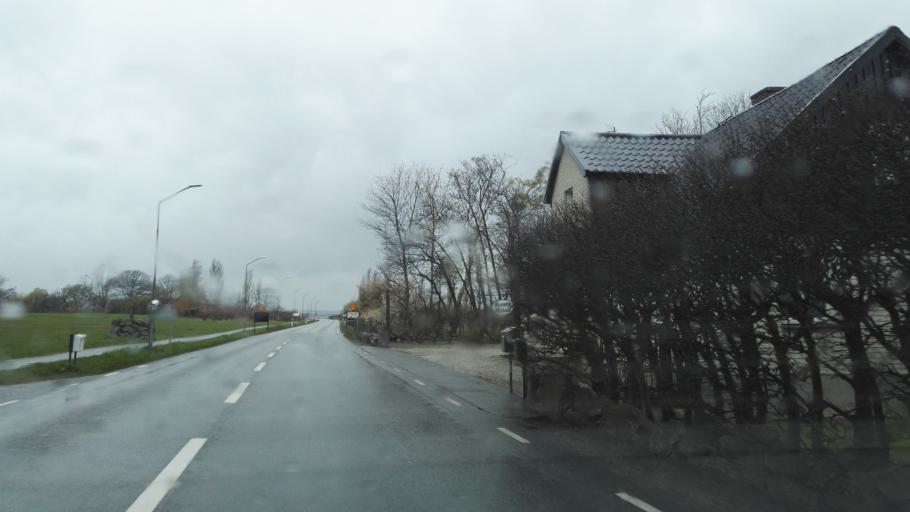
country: SE
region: Skane
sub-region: Simrishamns Kommun
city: Kivik
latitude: 55.6886
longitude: 14.2146
